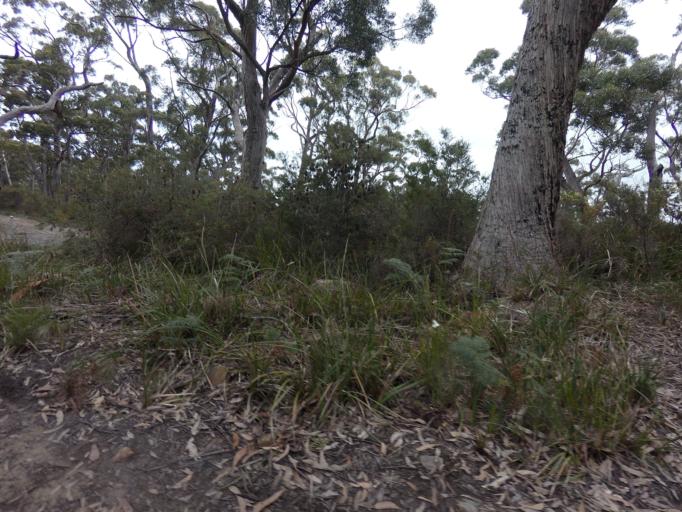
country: AU
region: Tasmania
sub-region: Huon Valley
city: Geeveston
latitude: -43.4686
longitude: 146.9320
